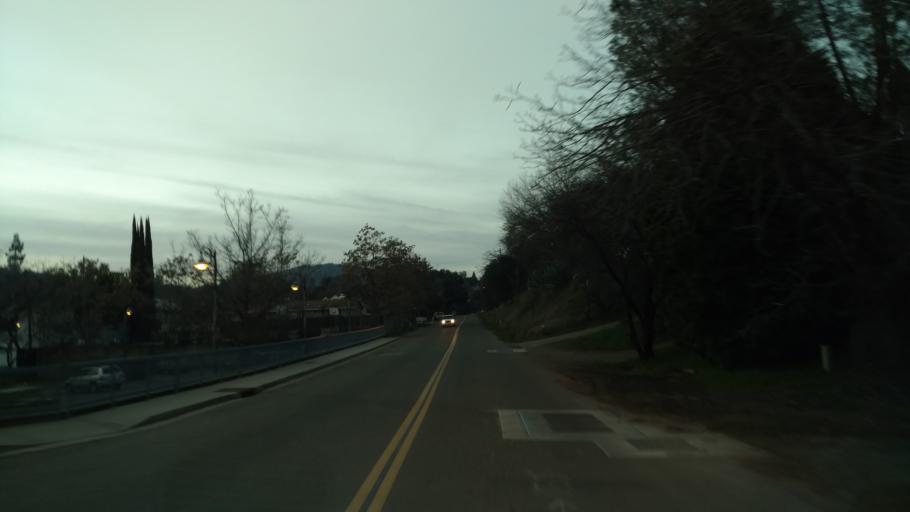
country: US
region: California
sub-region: Mariposa County
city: Mariposa
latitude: 37.4899
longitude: -119.9673
